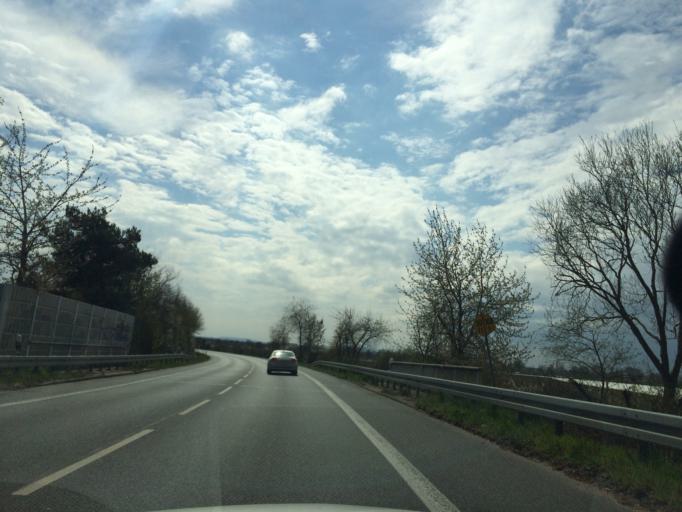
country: DE
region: Hesse
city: Weiterstadt
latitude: 49.9281
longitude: 8.5938
